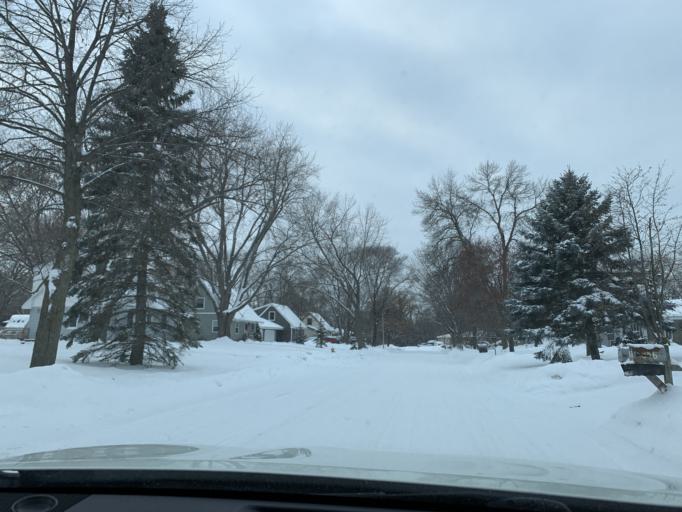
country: US
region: Minnesota
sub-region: Anoka County
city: Coon Rapids
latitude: 45.1737
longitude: -93.2890
